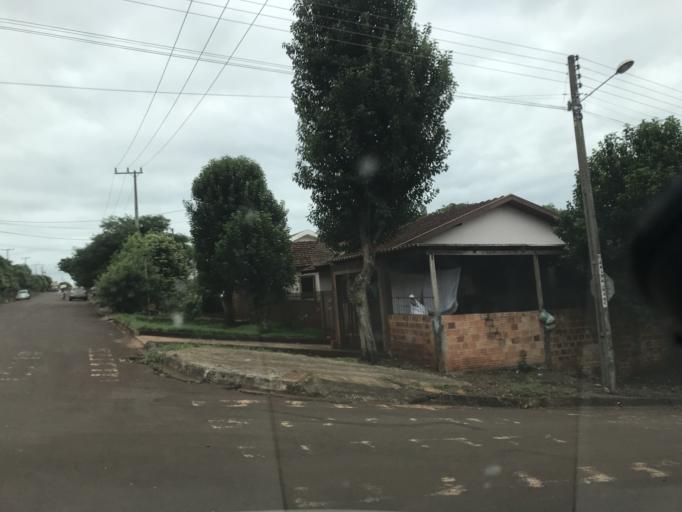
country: BR
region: Parana
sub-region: Palotina
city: Palotina
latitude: -24.3021
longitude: -53.8301
